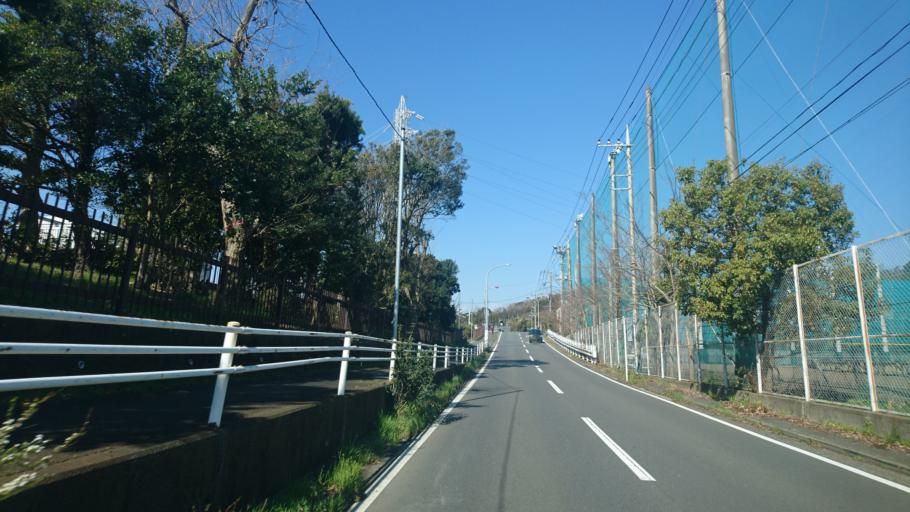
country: JP
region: Kanagawa
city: Fujisawa
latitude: 35.3615
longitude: 139.4876
